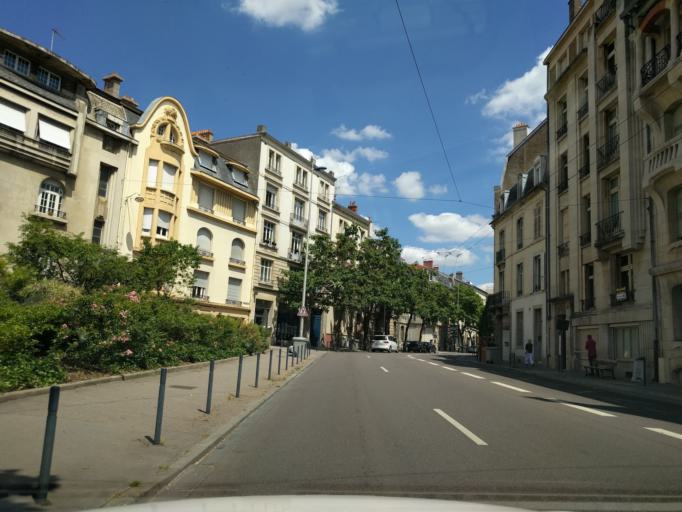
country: FR
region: Lorraine
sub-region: Departement de Meurthe-et-Moselle
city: Nancy
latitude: 48.6864
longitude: 6.1676
